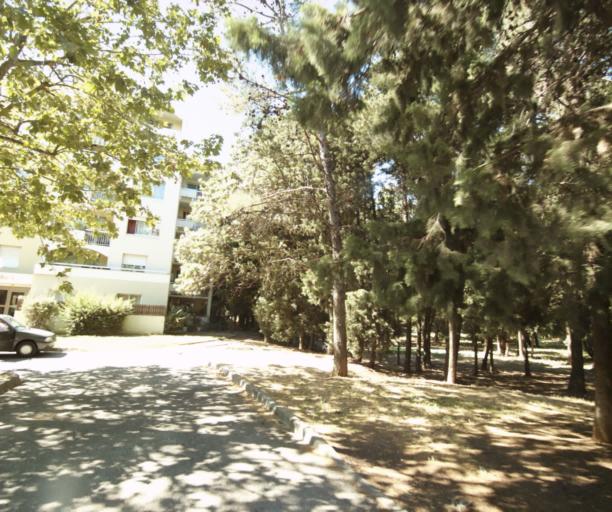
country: FR
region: Provence-Alpes-Cote d'Azur
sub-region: Departement du Var
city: La Garde
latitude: 43.1300
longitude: 6.0181
